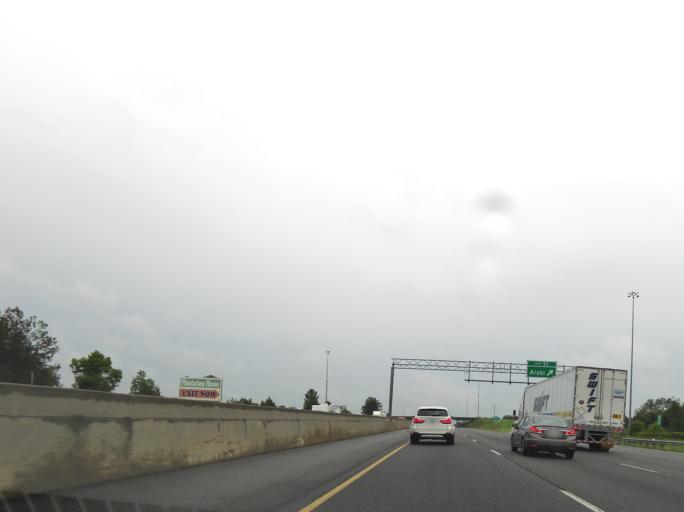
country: US
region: Georgia
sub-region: Crisp County
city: Cordele
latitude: 31.8391
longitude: -83.7149
